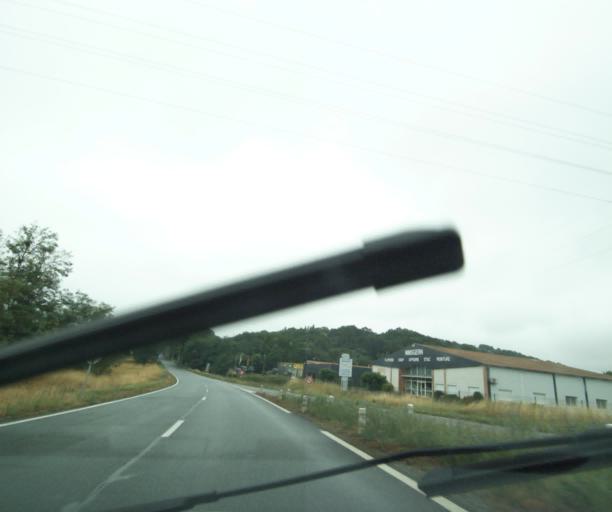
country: FR
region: Midi-Pyrenees
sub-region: Departement du Tarn
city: Arthes
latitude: 43.9712
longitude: 2.1831
